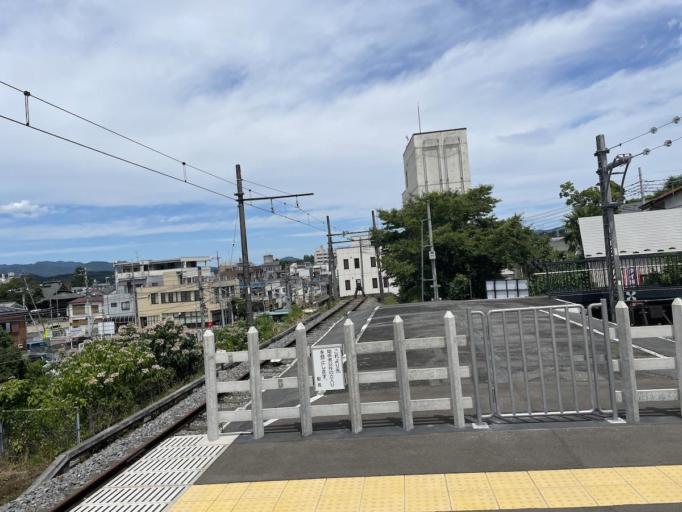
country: JP
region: Saitama
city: Chichibu
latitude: 35.9909
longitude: 139.0834
